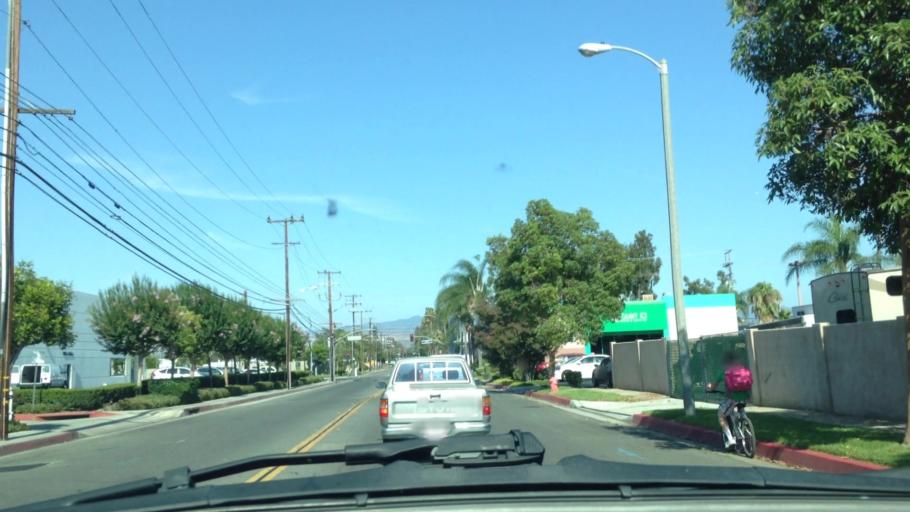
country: US
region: California
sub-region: Orange County
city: Orange
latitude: 33.8060
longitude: -117.8687
